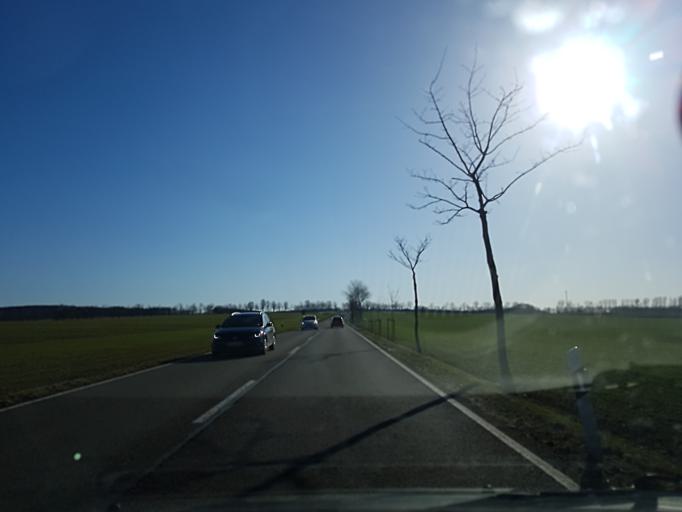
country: DE
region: Saxony
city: Frankenstein
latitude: 50.8822
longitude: 13.2274
